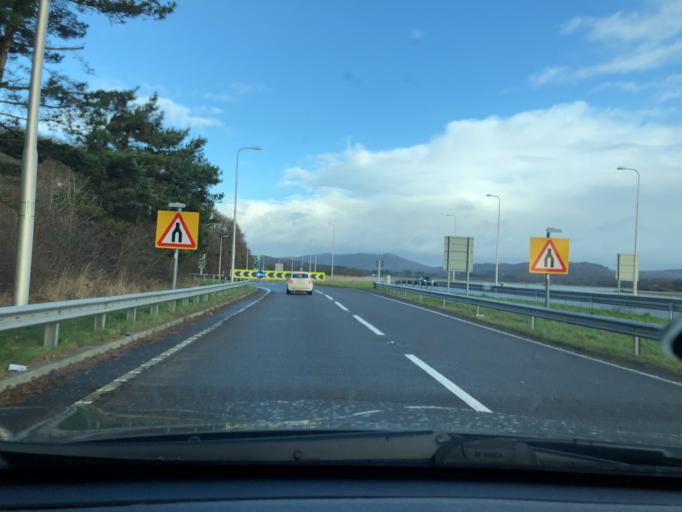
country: GB
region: England
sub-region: Cumbria
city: Ulverston
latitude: 54.2344
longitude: -3.0509
